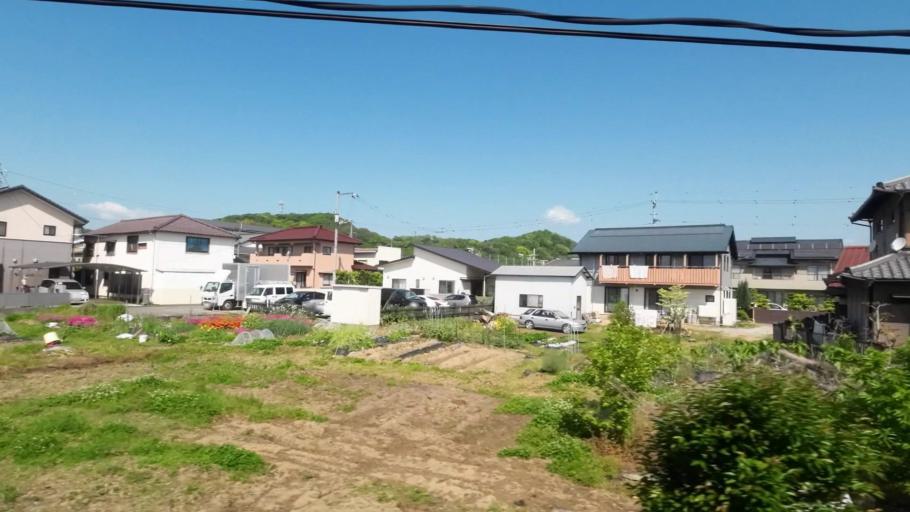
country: JP
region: Kagawa
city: Tadotsu
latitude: 34.2638
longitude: 133.7530
